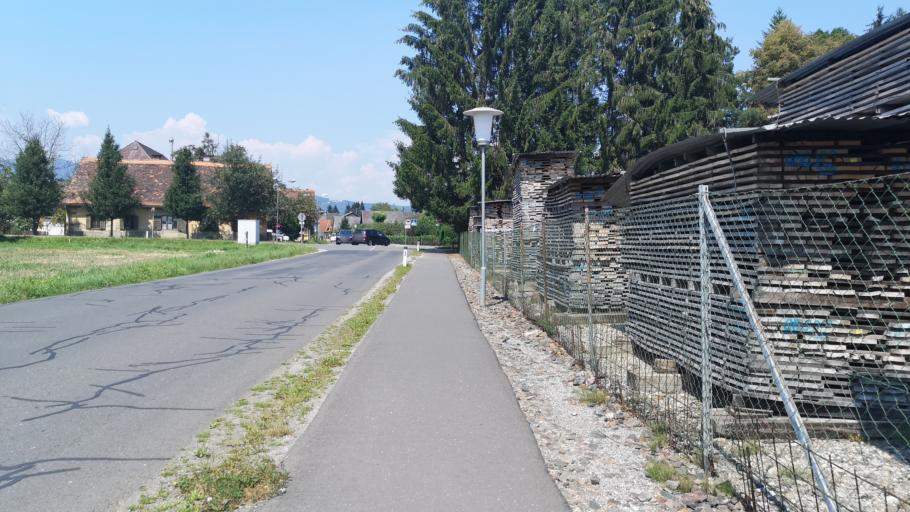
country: AT
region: Styria
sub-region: Politischer Bezirk Deutschlandsberg
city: Deutschlandsberg
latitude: 46.8211
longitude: 15.2555
